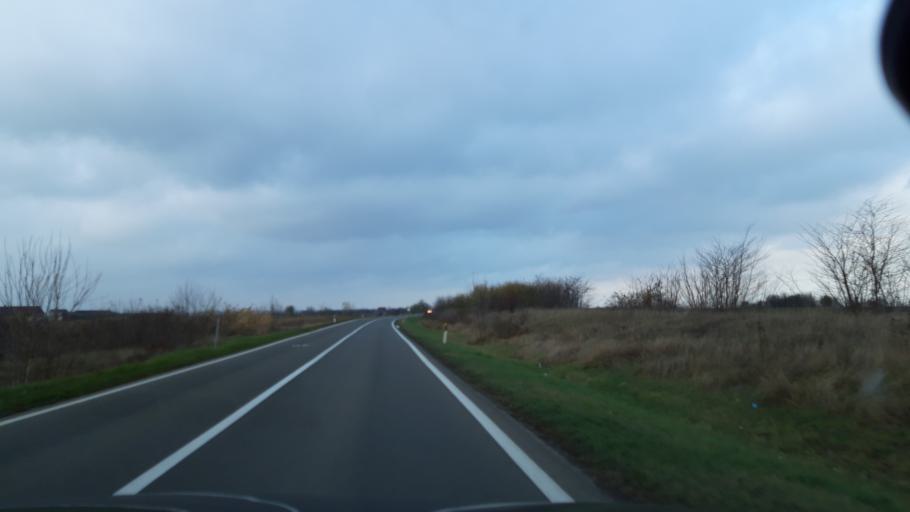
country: RS
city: Sanad
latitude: 45.9886
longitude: 20.1099
